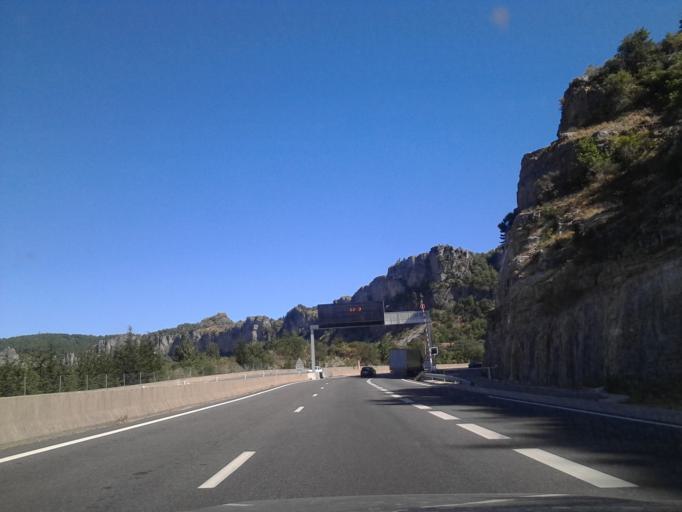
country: FR
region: Languedoc-Roussillon
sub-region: Departement de l'Herault
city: Lodeve
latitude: 43.8191
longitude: 3.3191
